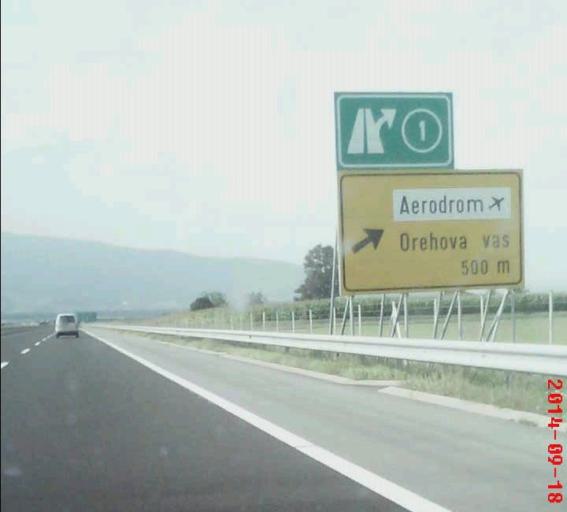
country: SI
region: Race-Fram
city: Race
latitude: 46.4682
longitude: 15.6874
